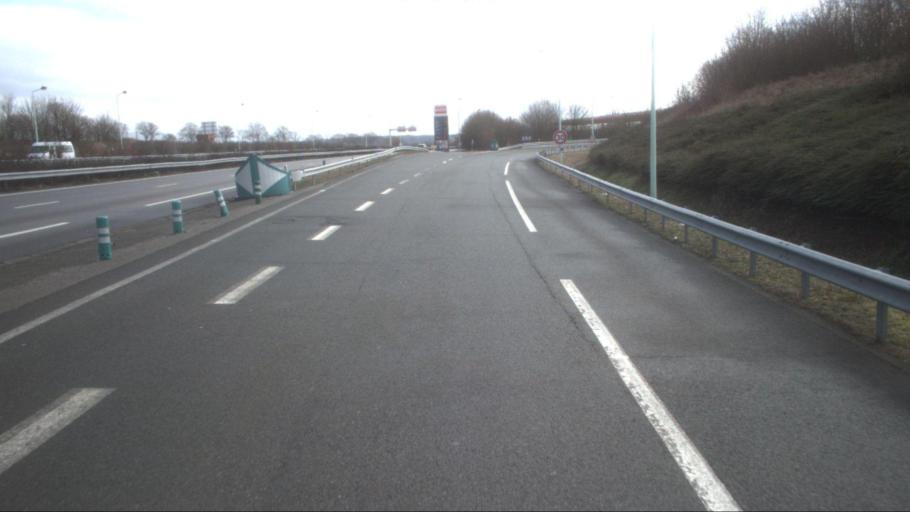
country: FR
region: Ile-de-France
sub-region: Departement des Yvelines
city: Houdan
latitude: 48.7916
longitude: 1.6321
